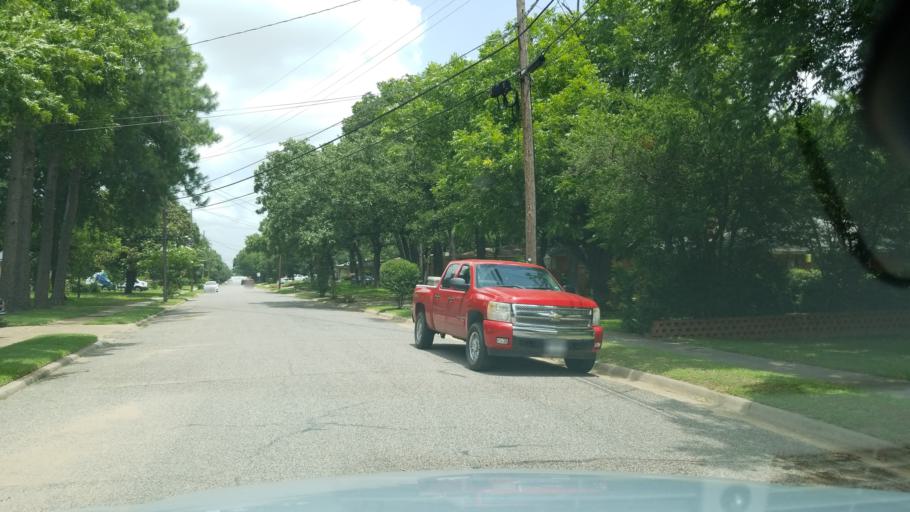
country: US
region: Texas
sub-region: Dallas County
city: Irving
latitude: 32.8313
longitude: -96.9243
